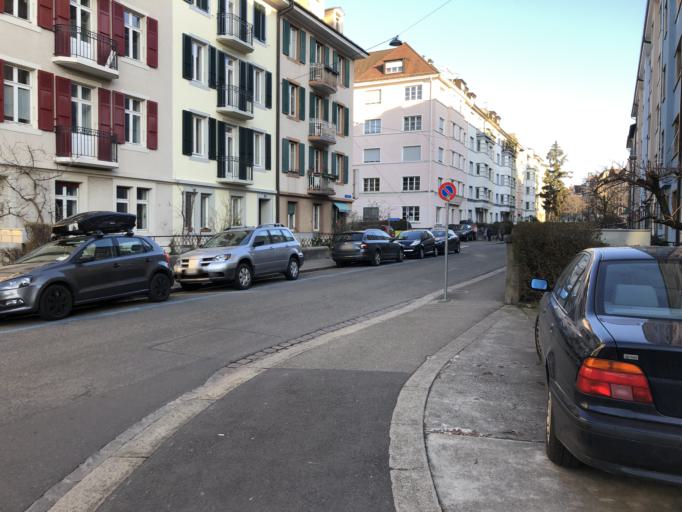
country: CH
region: Basel-City
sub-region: Basel-Stadt
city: Basel
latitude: 47.5583
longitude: 7.5715
